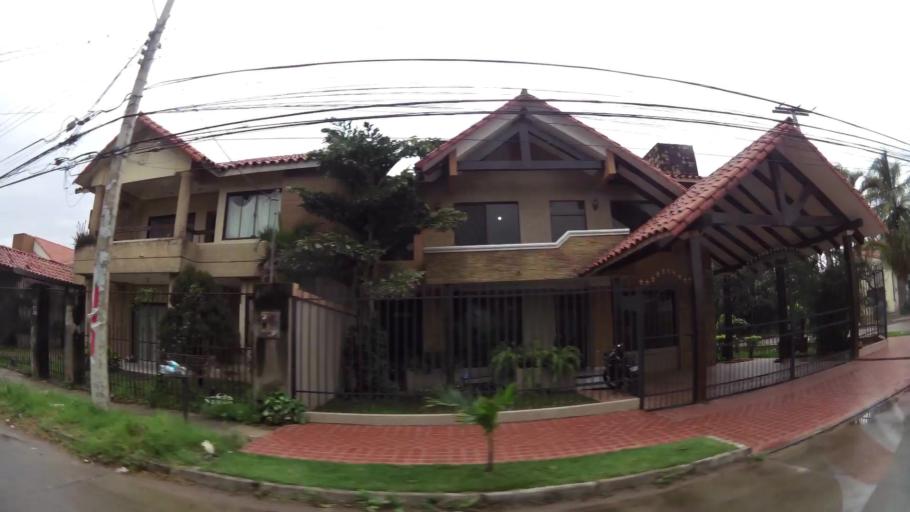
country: BO
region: Santa Cruz
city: Santa Cruz de la Sierra
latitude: -17.7815
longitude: -63.1326
